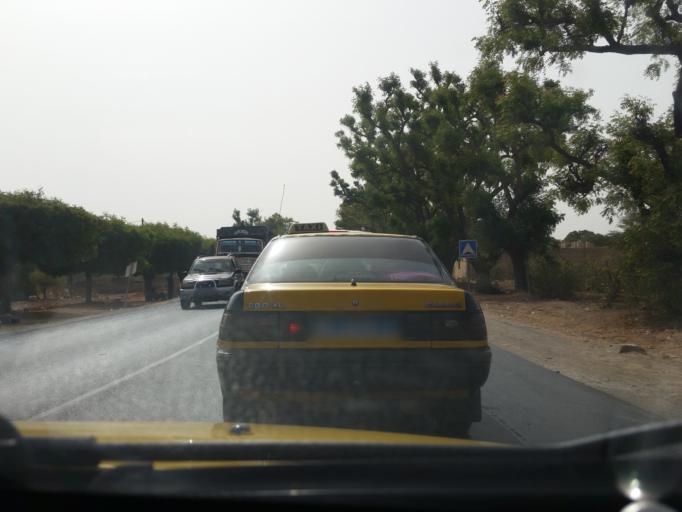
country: SN
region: Thies
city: Pout
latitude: 14.7618
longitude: -17.0388
